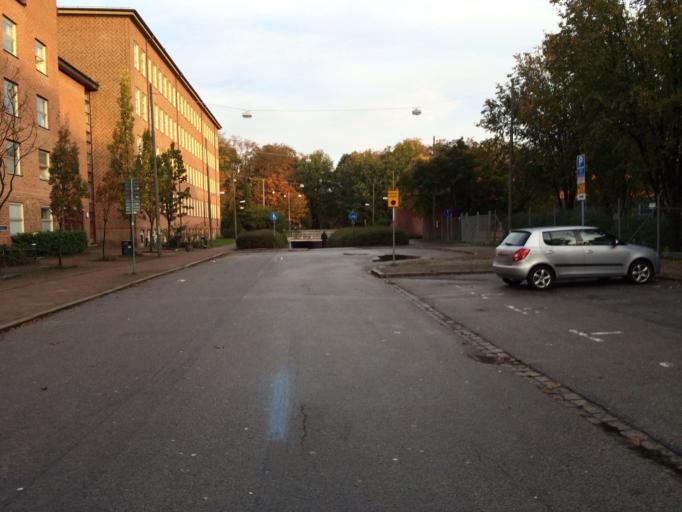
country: SE
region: Skane
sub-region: Malmo
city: Malmoe
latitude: 55.5986
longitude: 12.9917
